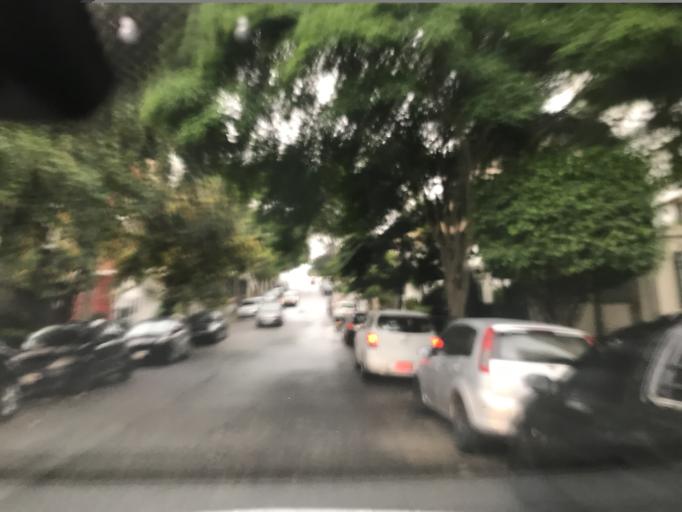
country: BR
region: Sao Paulo
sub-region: Sao Paulo
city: Sao Paulo
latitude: -23.5351
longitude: -46.6857
